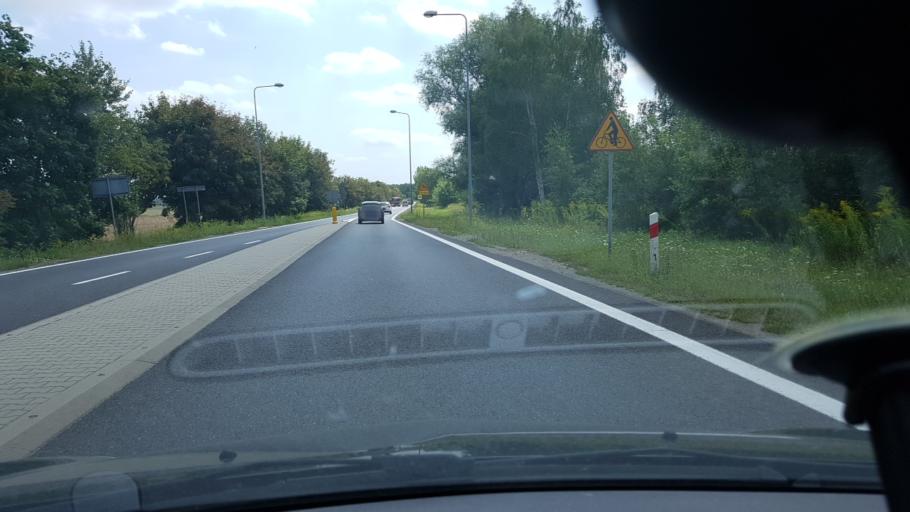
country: PL
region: Silesian Voivodeship
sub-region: Powiat bierunsko-ledzinski
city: Bierun
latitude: 50.0914
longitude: 19.1054
